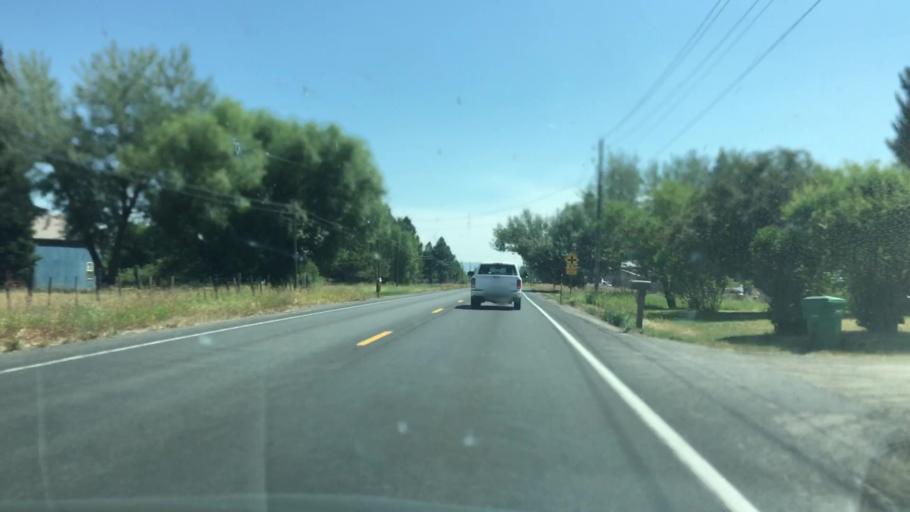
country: US
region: Idaho
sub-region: Valley County
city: McCall
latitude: 44.8495
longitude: -116.0904
